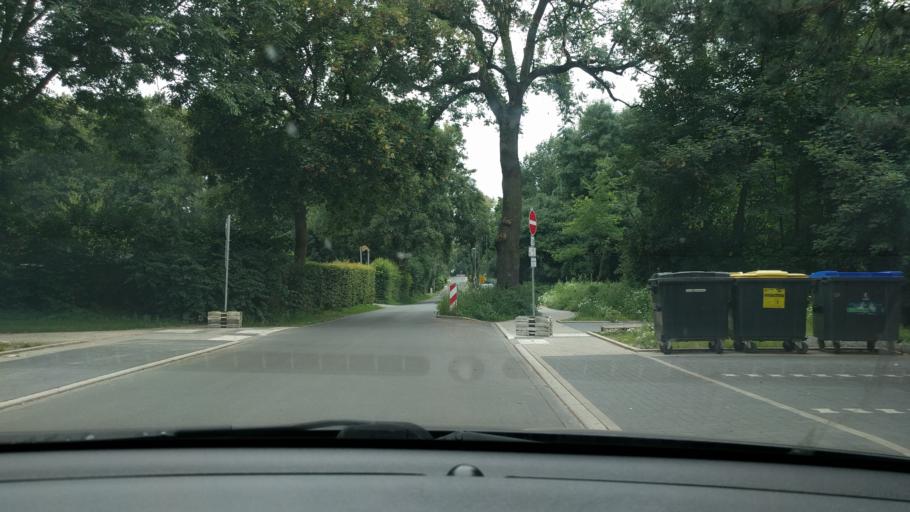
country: DE
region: North Rhine-Westphalia
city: Witten
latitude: 51.4772
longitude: 7.3293
